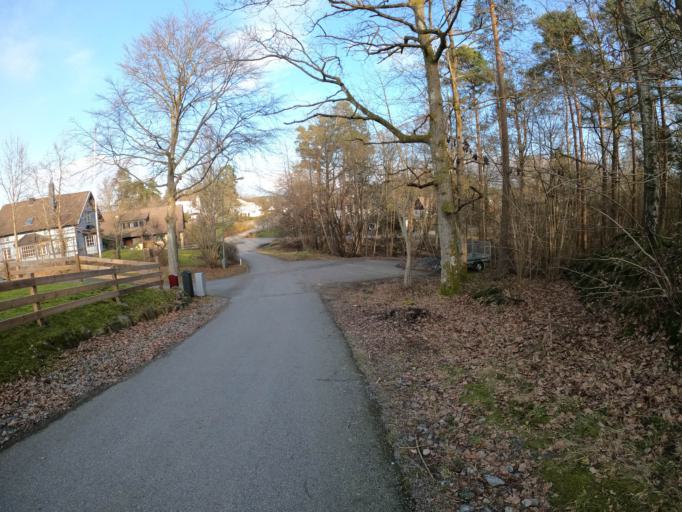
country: SE
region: Vaestra Goetaland
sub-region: Harryda Kommun
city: Molnlycke
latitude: 57.6538
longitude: 12.1195
